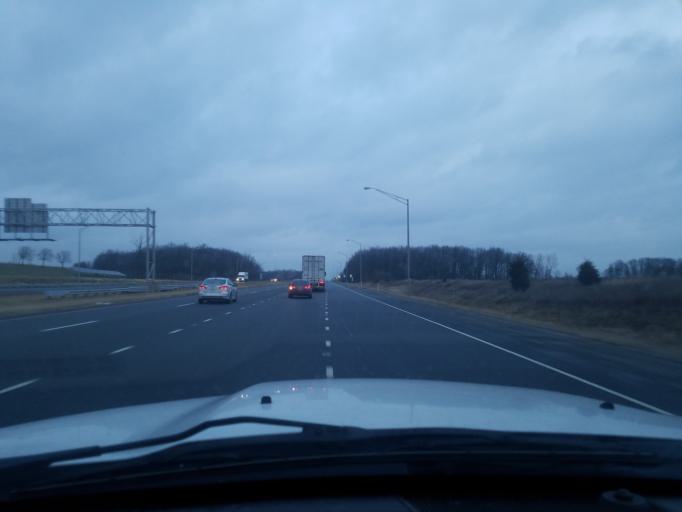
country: US
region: Indiana
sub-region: Huntington County
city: Roanoke
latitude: 40.9654
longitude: -85.2877
